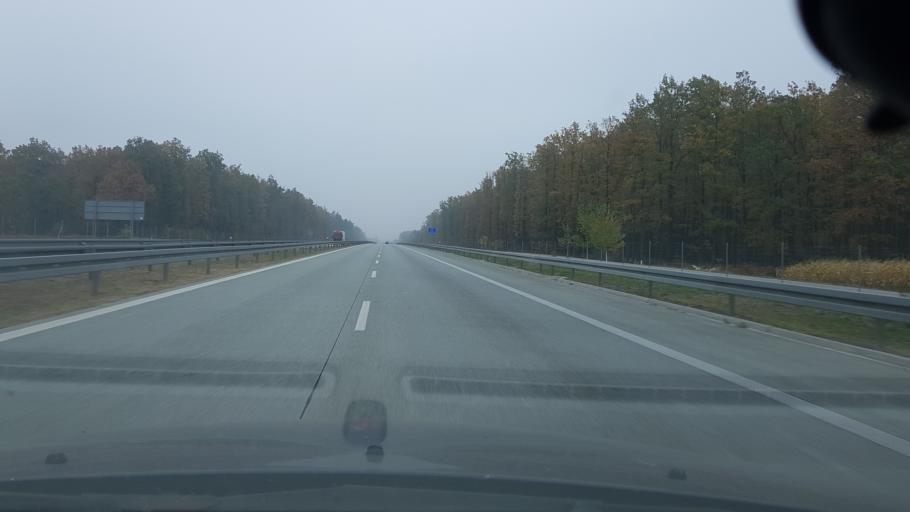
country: PL
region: Lodz Voivodeship
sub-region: Powiat rawski
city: Rawa Mazowiecka
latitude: 51.7204
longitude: 20.2230
